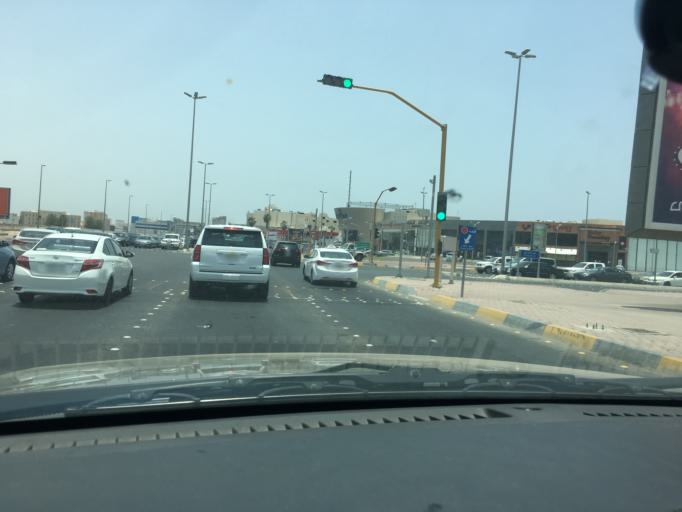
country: SA
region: Makkah
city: Jeddah
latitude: 21.5979
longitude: 39.1442
